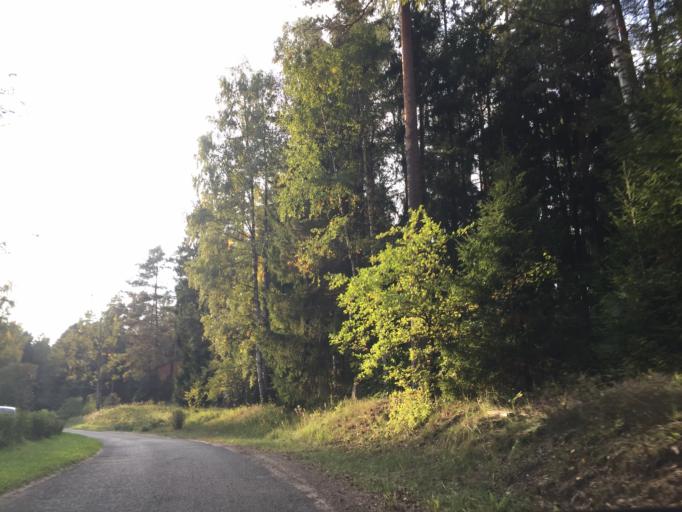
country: LV
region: Baldone
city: Baldone
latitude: 56.7746
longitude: 24.4123
